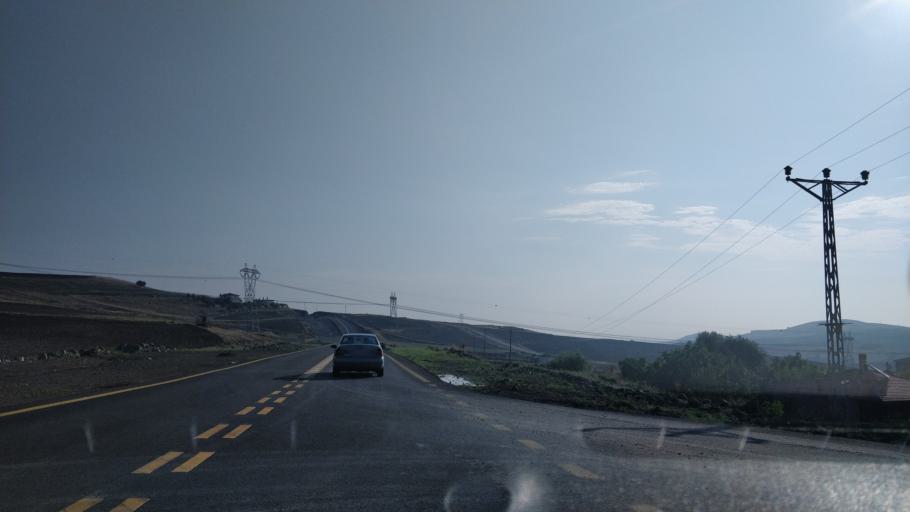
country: TR
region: Ankara
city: Etimesgut
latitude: 39.8636
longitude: 32.5846
